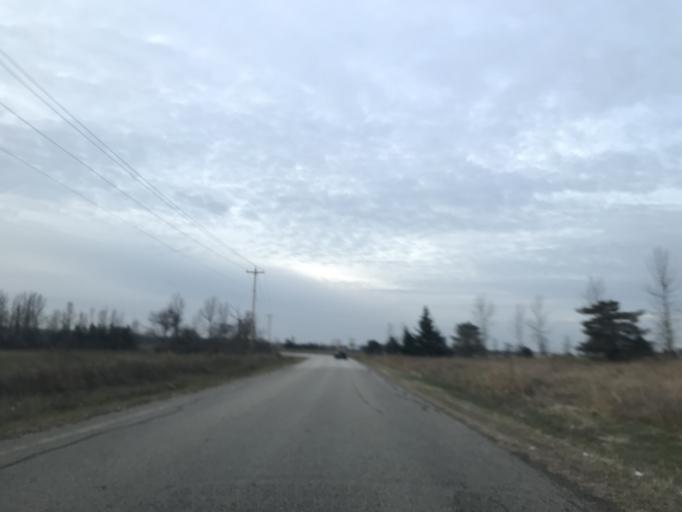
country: US
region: Wisconsin
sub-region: Marinette County
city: Peshtigo
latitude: 45.0543
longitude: -87.7990
